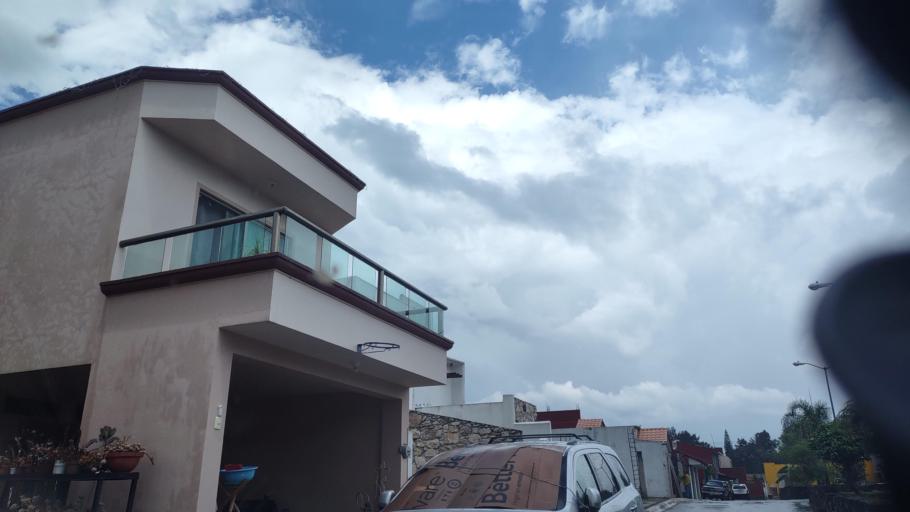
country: MX
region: Veracruz
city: Coatepec
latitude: 19.4510
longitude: -96.9393
